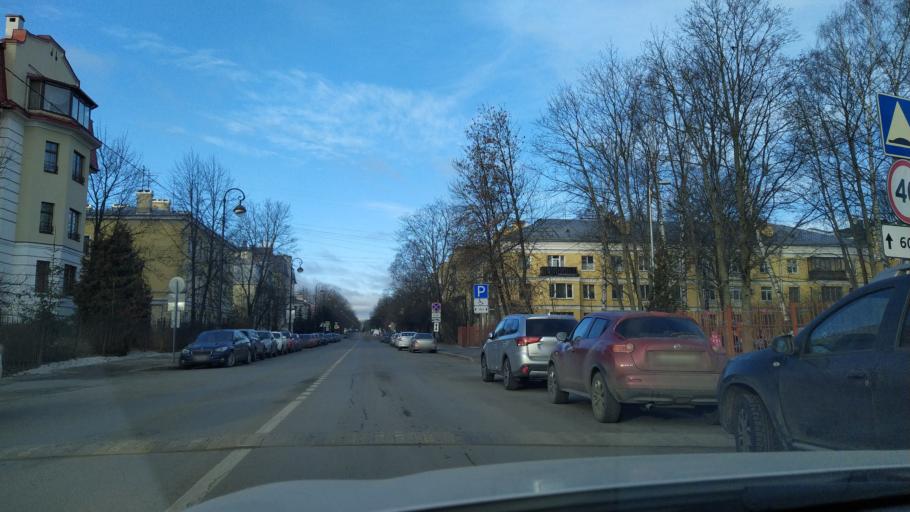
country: RU
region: St.-Petersburg
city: Pushkin
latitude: 59.7186
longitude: 30.4159
